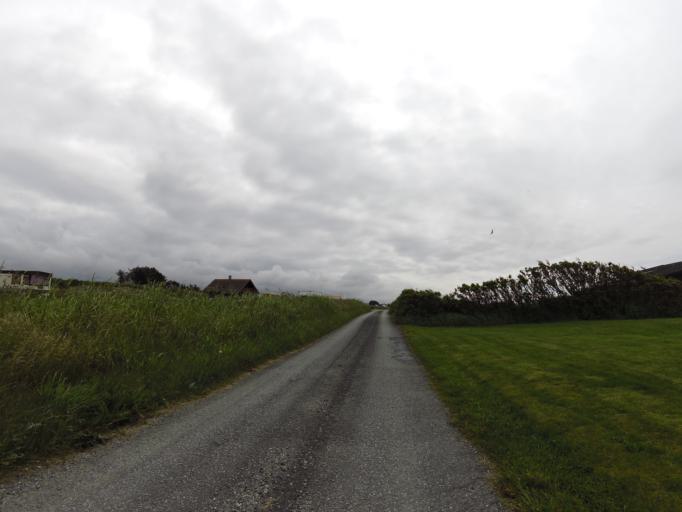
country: NO
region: Rogaland
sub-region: Klepp
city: Kleppe
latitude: 58.8143
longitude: 5.5490
